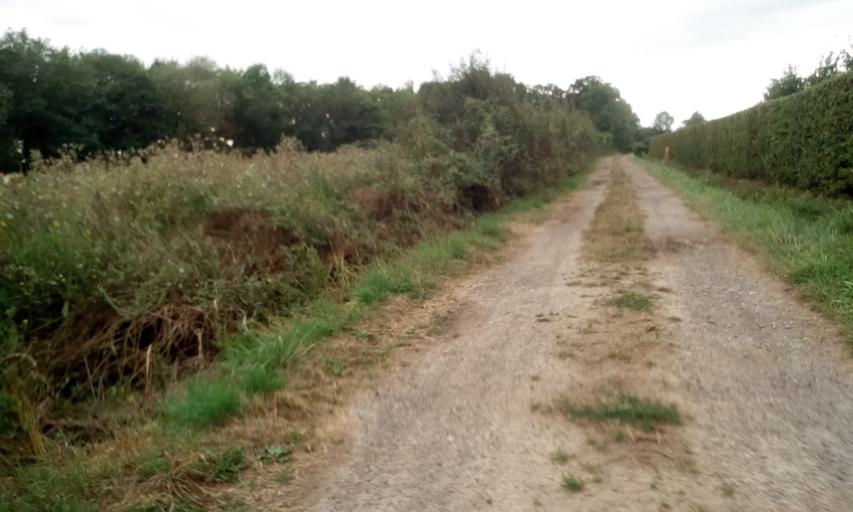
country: FR
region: Lower Normandy
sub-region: Departement du Calvados
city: Sannerville
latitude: 49.1854
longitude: -0.2062
